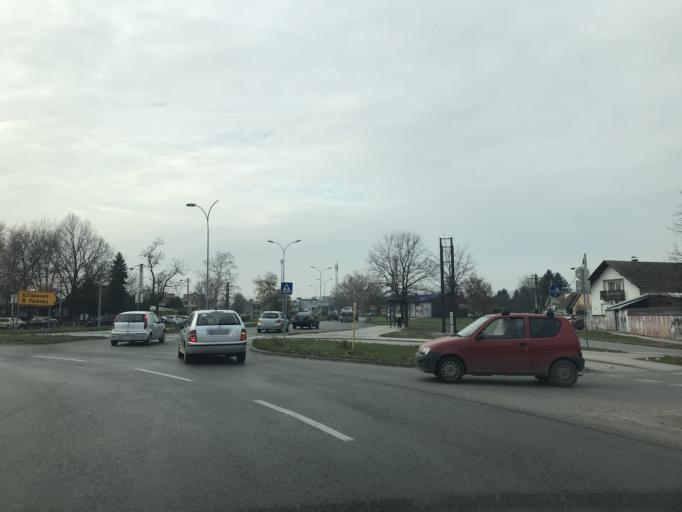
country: RS
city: Veternik
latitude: 45.2498
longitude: 19.7563
